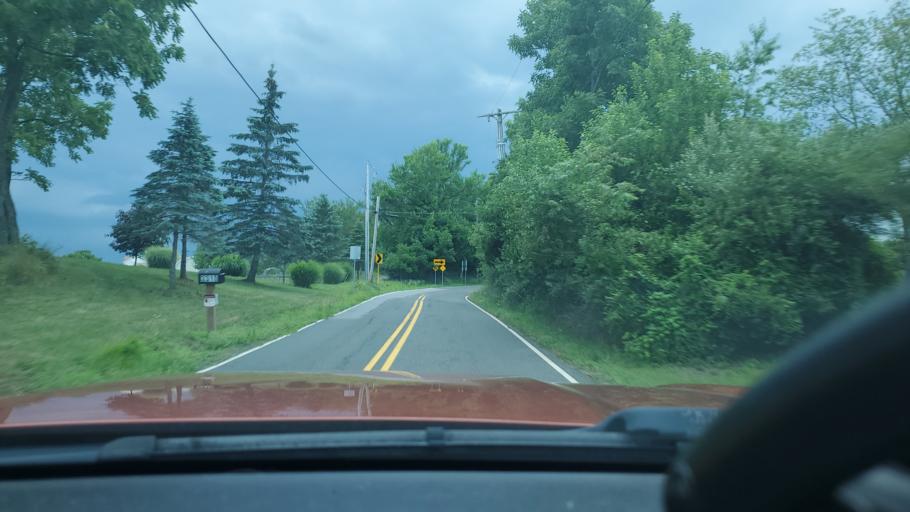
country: US
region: Pennsylvania
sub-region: Montgomery County
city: Limerick
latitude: 40.2797
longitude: -75.5231
